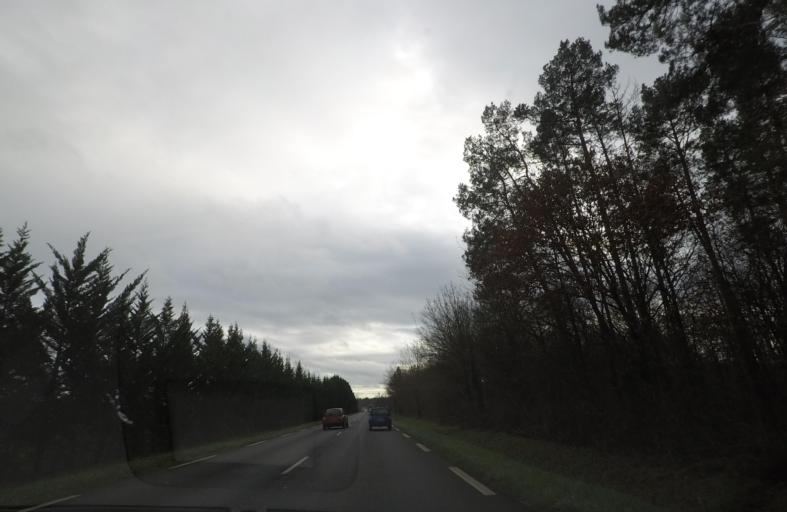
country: FR
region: Centre
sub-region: Departement du Loir-et-Cher
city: Mur-de-Sologne
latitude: 47.4011
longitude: 1.6335
